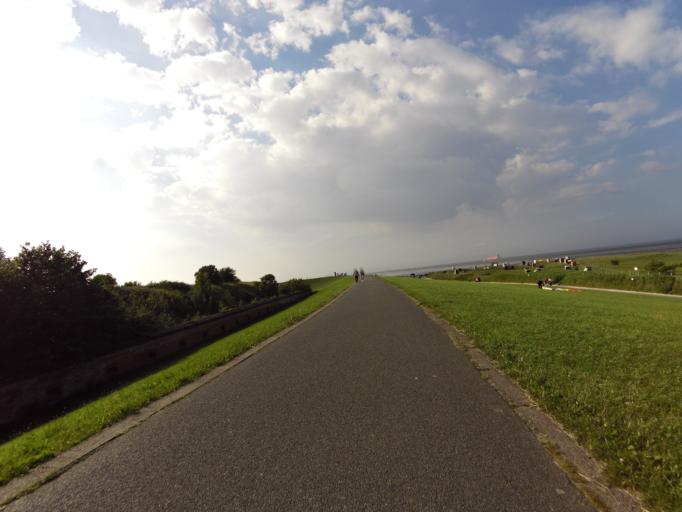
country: DE
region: Lower Saxony
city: Cuxhaven
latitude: 53.8903
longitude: 8.6828
